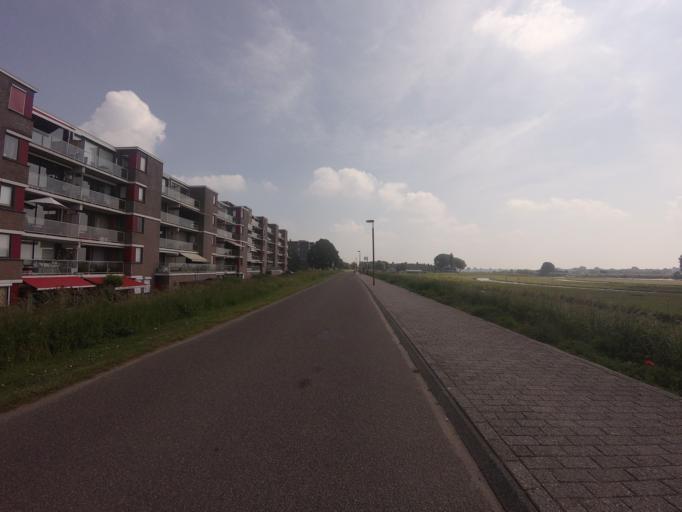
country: NL
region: Utrecht
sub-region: Gemeente Vianen
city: Vianen
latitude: 52.0023
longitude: 5.0804
